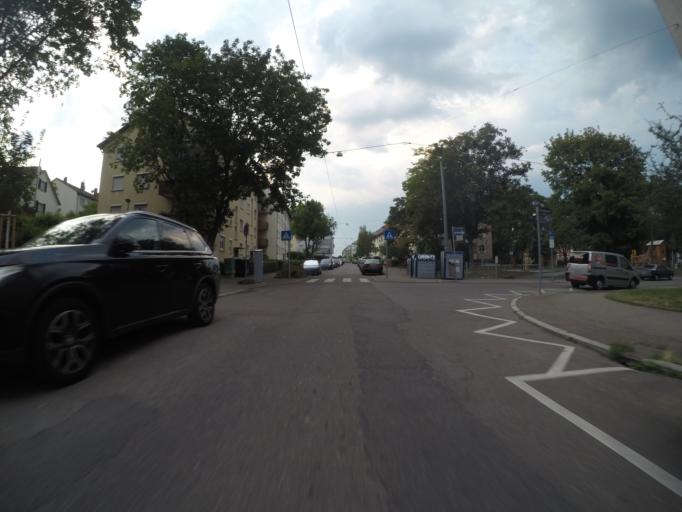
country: DE
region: Baden-Wuerttemberg
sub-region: Regierungsbezirk Stuttgart
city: Stuttgart-Ost
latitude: 48.7823
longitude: 9.2050
